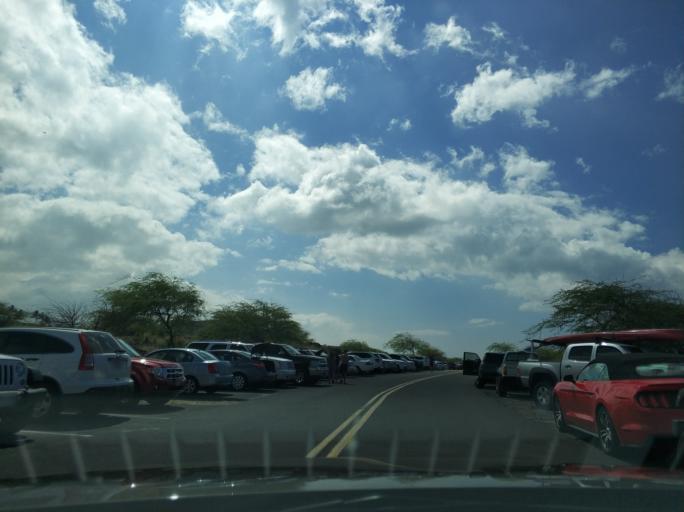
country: US
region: Hawaii
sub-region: Hawaii County
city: Kalaoa
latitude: 19.8093
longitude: -156.0061
